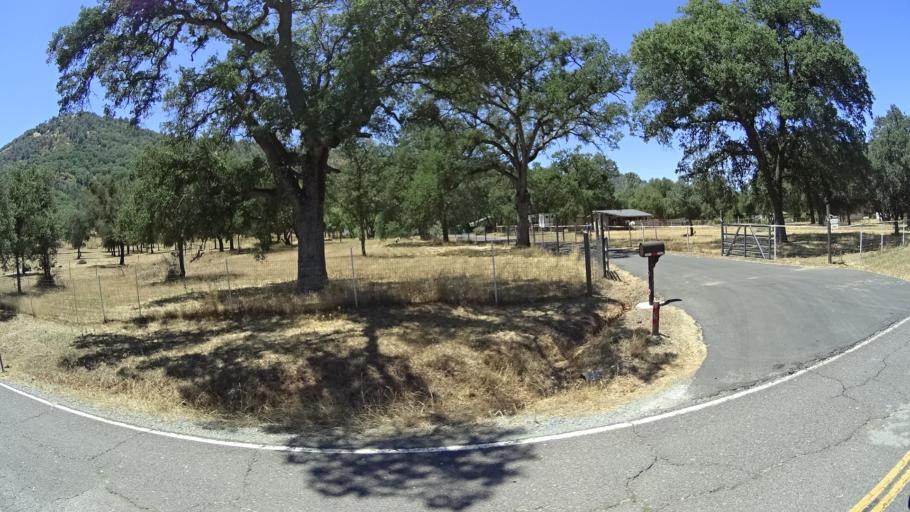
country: US
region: California
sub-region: Calaveras County
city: Copperopolis
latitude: 38.0619
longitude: -120.6541
